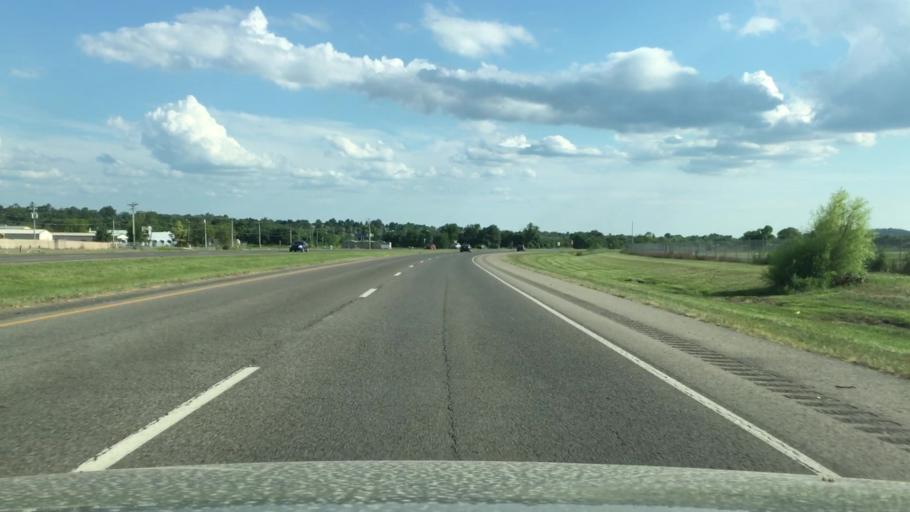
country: US
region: Oklahoma
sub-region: Cherokee County
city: Tahlequah
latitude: 35.9279
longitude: -95.0012
